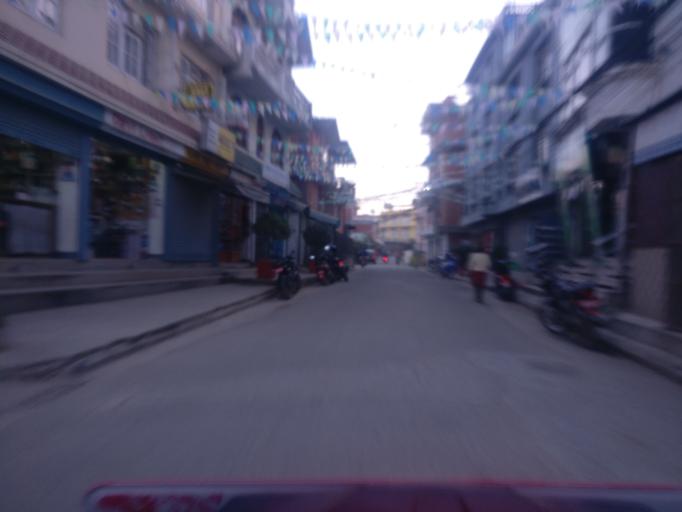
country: NP
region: Central Region
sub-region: Bagmati Zone
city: Patan
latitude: 27.6518
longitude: 85.3183
